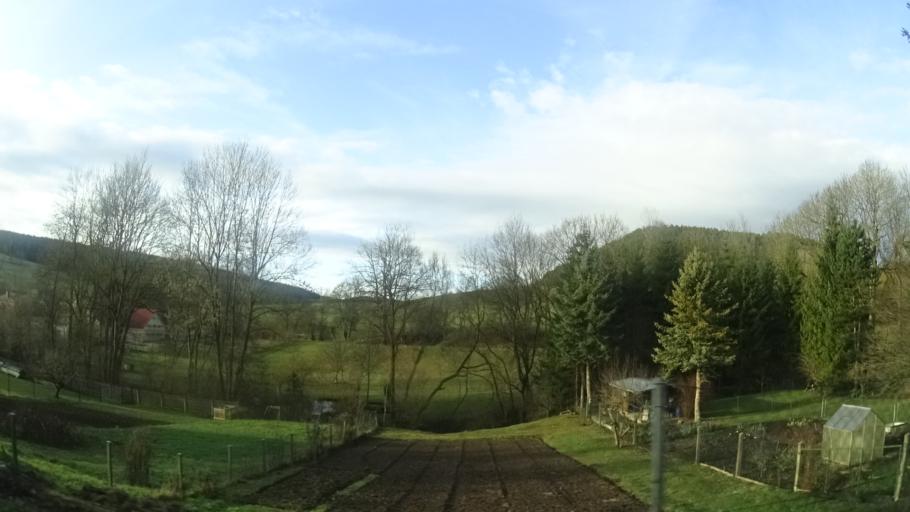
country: DE
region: Thuringia
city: Rottenbach
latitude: 50.7190
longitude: 11.1981
